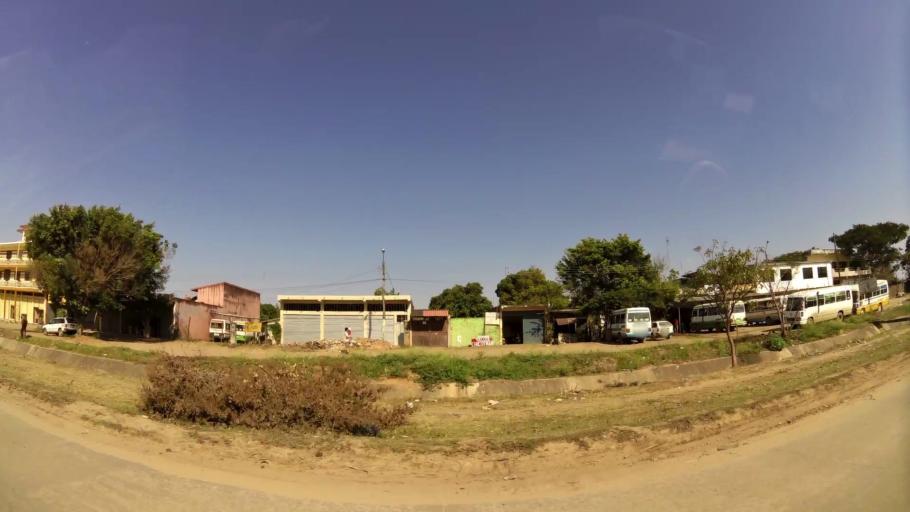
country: BO
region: Santa Cruz
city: Cotoca
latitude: -17.8155
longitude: -63.1131
